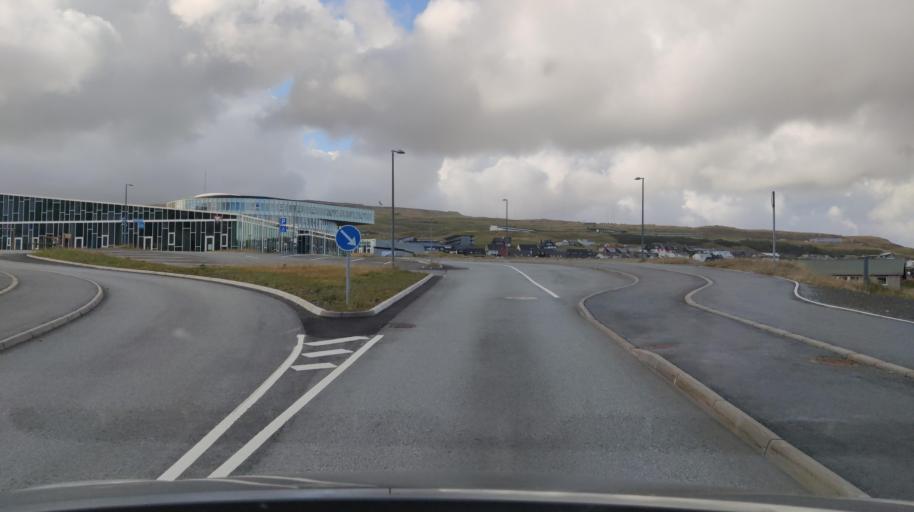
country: FO
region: Streymoy
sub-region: Torshavn
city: Torshavn
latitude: 62.0045
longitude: -6.7954
